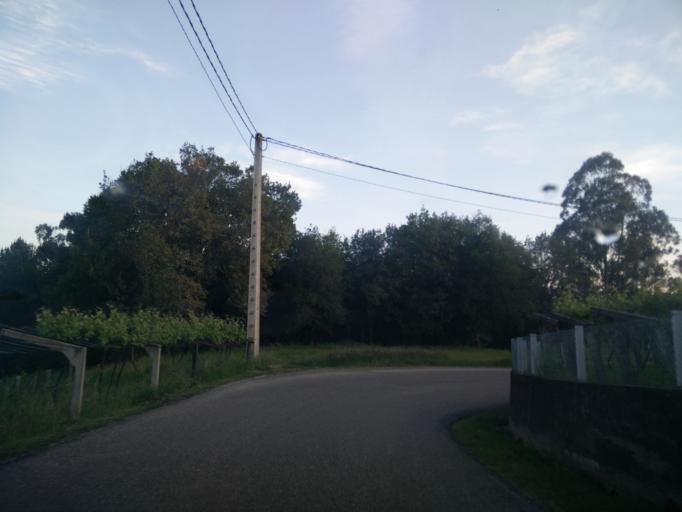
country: ES
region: Galicia
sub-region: Provincia de Pontevedra
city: Mondariz
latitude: 42.2525
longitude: -8.4242
